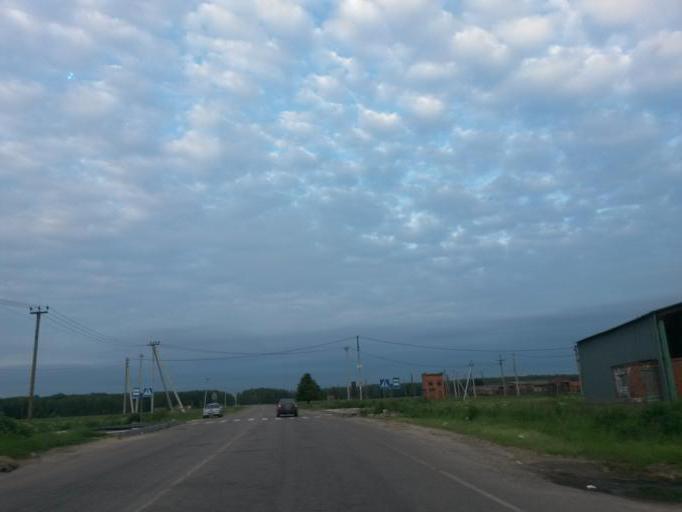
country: RU
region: Moskovskaya
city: Lyubuchany
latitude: 55.2482
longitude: 37.5560
